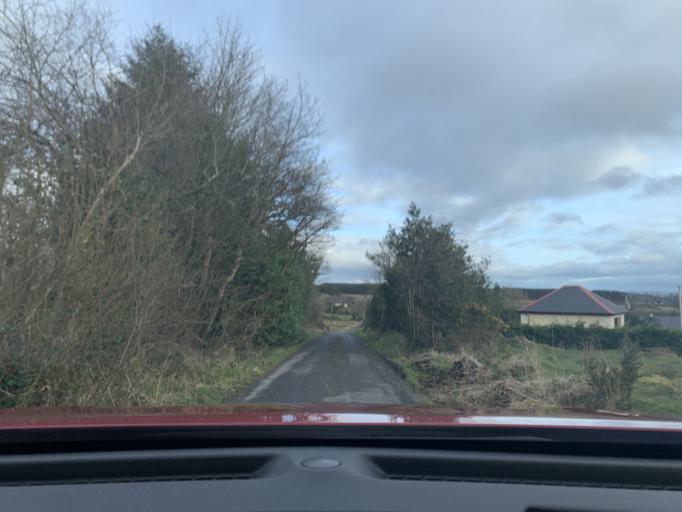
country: IE
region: Connaught
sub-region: Roscommon
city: Ballaghaderreen
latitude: 53.9344
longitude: -8.5458
